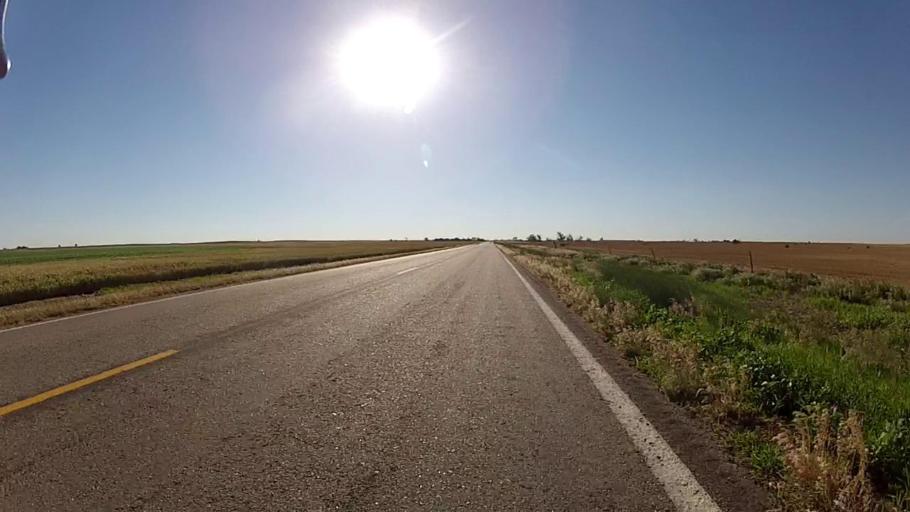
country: US
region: Kansas
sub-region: Ford County
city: Dodge City
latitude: 37.6459
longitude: -99.8105
